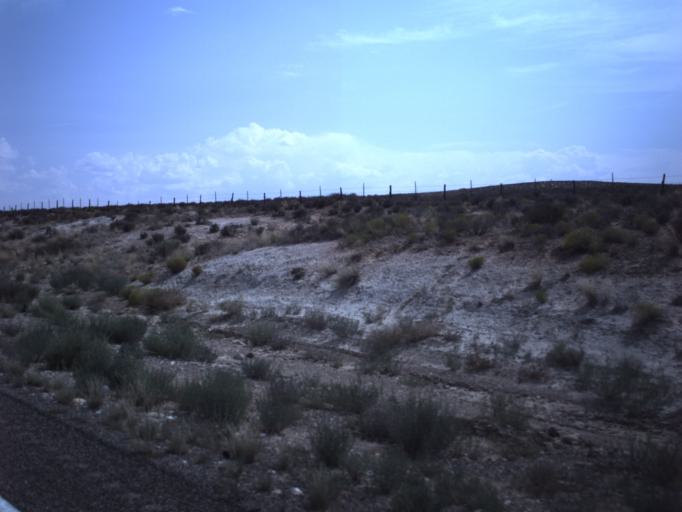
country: US
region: Arizona
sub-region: Coconino County
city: Page
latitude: 37.0033
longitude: -111.5748
